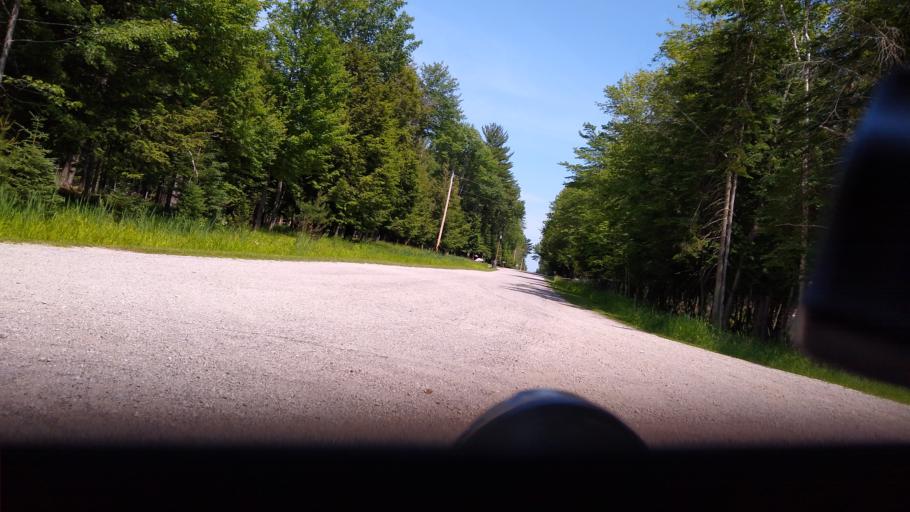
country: US
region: Michigan
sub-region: Delta County
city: Escanaba
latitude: 45.7098
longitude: -87.1601
